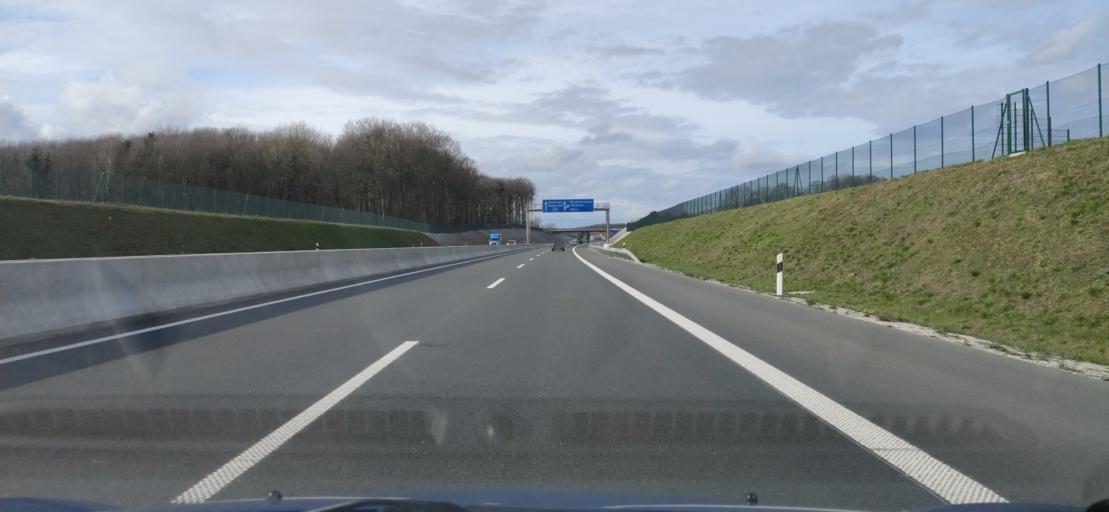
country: DE
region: North Rhine-Westphalia
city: Borgholzhausen
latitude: 52.0706
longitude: 8.2579
